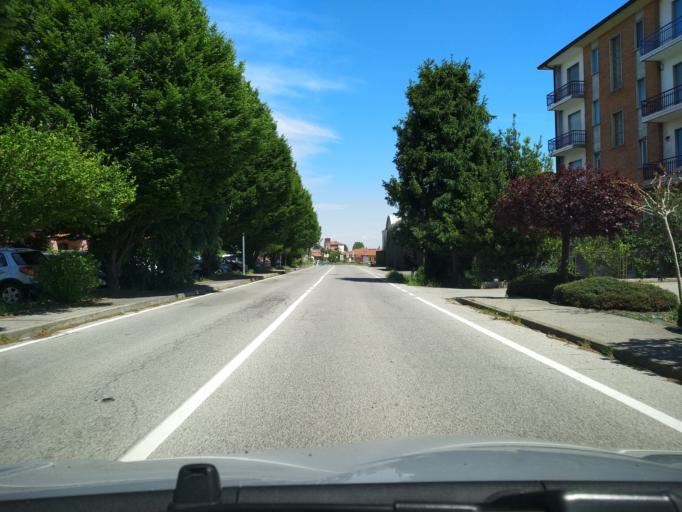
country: IT
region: Piedmont
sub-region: Provincia di Torino
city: Riva
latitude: 44.8917
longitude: 7.3796
